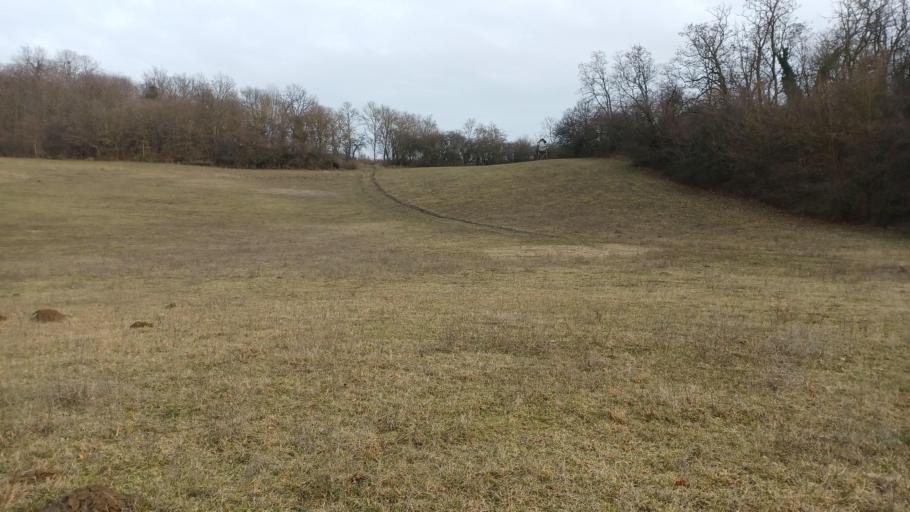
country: HU
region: Tolna
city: Szentgalpuszta
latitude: 46.3012
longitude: 18.6160
